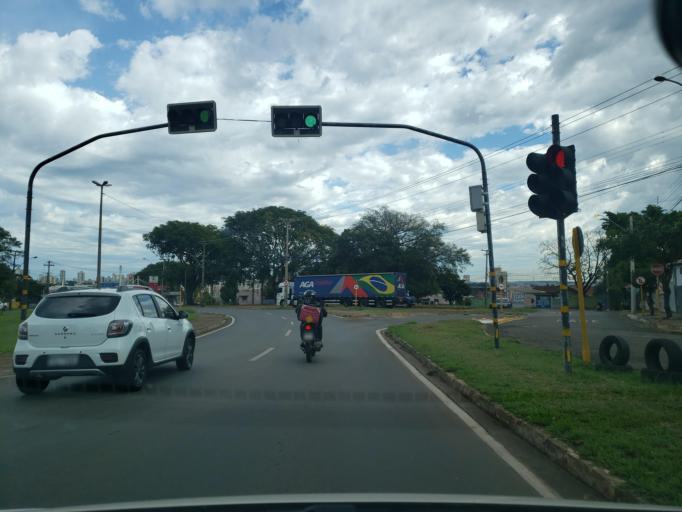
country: BR
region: Sao Paulo
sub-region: Bauru
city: Bauru
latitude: -22.3353
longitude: -49.0312
